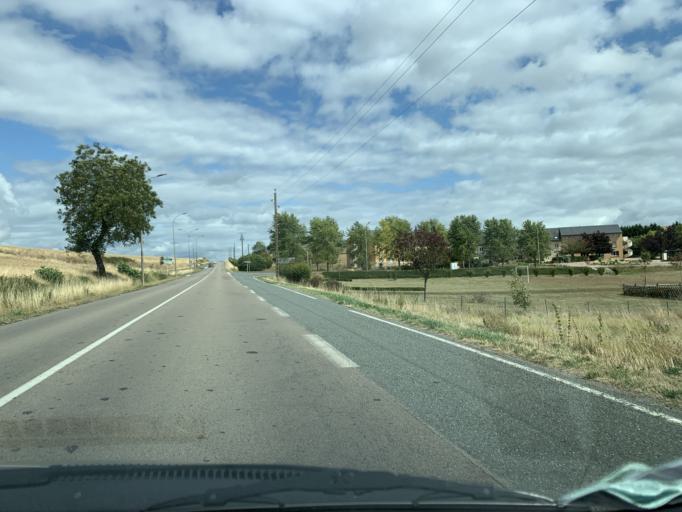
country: FR
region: Bourgogne
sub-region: Departement de la Nievre
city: Varzy
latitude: 47.3619
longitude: 3.4026
